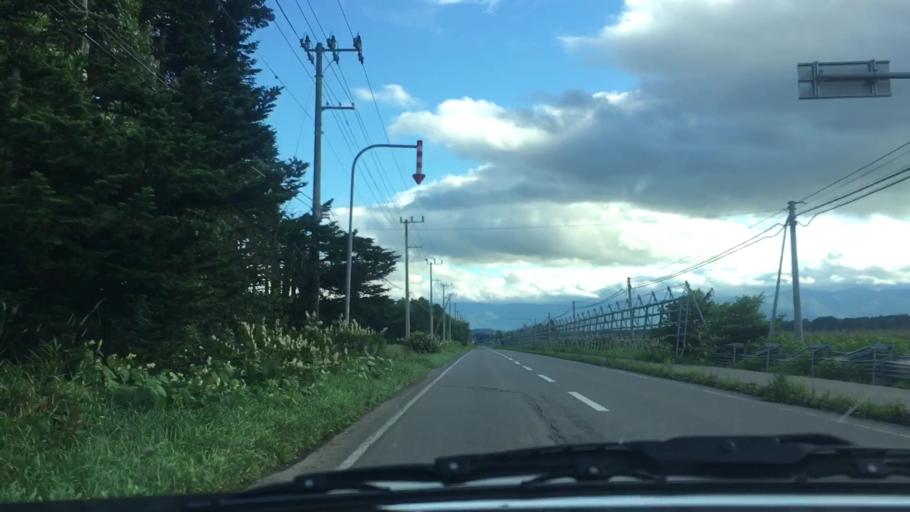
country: JP
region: Hokkaido
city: Otofuke
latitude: 43.1440
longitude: 142.8972
